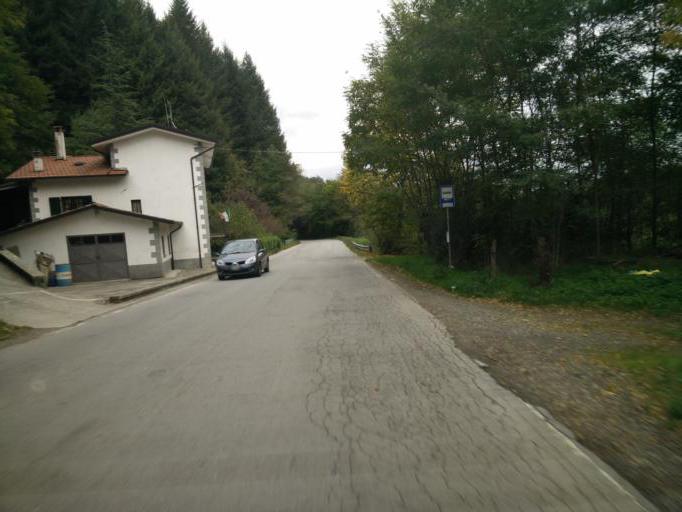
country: IT
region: Tuscany
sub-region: Provincia di Lucca
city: Camporgiano
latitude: 44.1729
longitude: 10.3212
